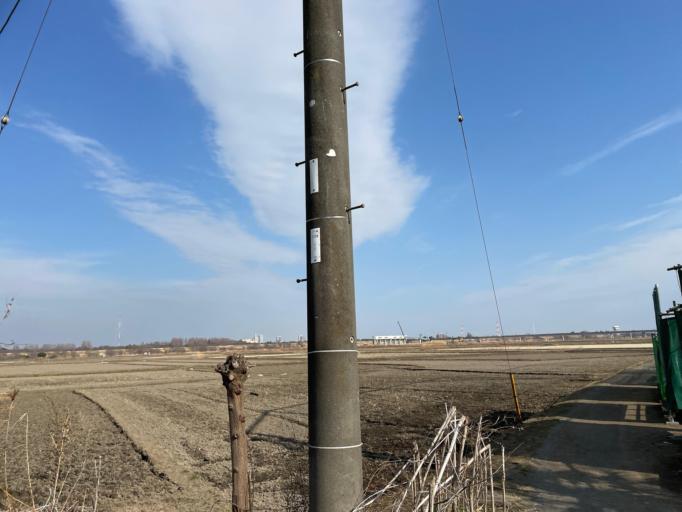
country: JP
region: Saitama
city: Shiki
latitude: 35.8419
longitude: 139.5957
